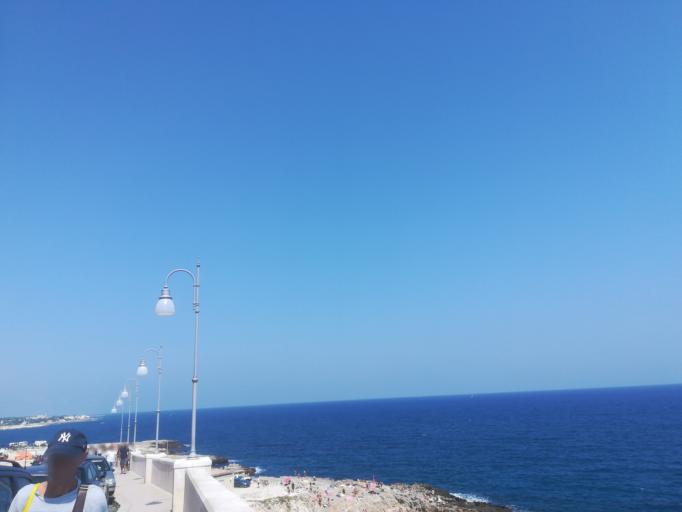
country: IT
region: Apulia
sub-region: Provincia di Bari
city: Polignano a Mare
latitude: 40.9979
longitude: 17.2163
